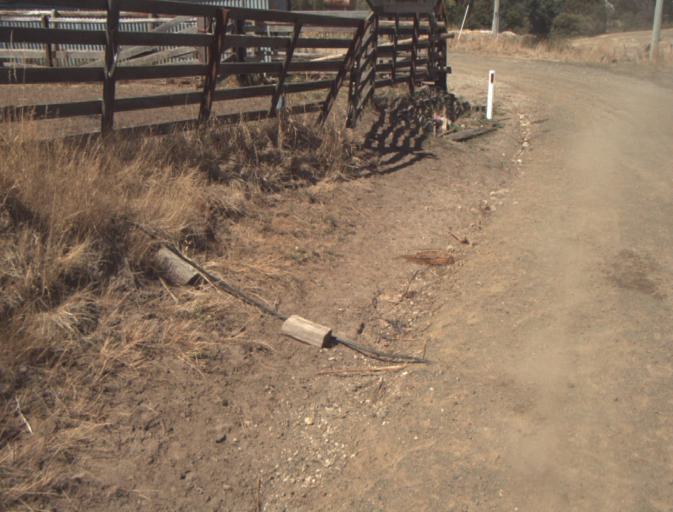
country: AU
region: Tasmania
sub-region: Launceston
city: Mayfield
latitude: -41.2525
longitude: 147.1736
